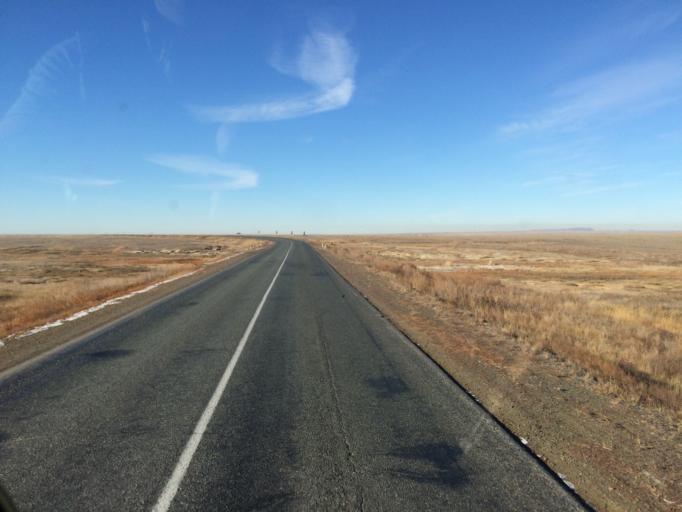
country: KZ
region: Aqtoebe
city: Khromtau
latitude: 50.1857
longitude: 58.6714
